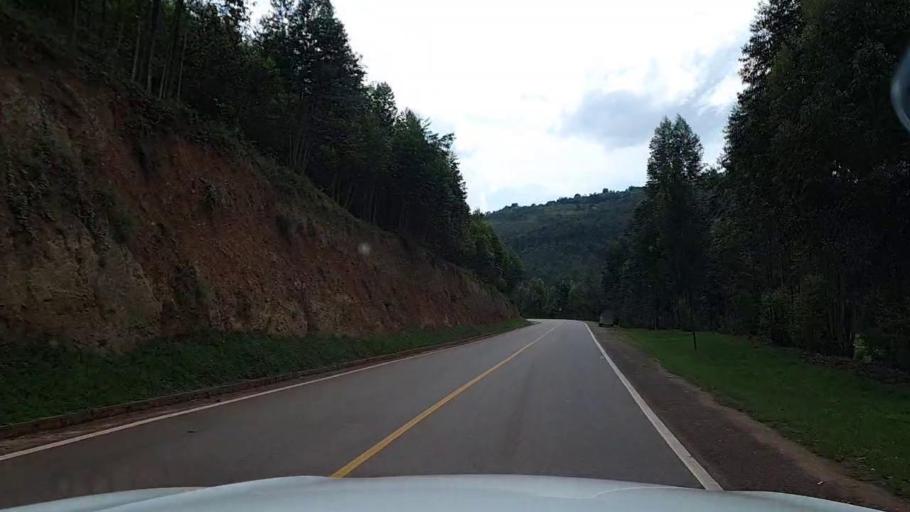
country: RW
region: Kigali
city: Kigali
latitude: -1.8185
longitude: 30.1121
